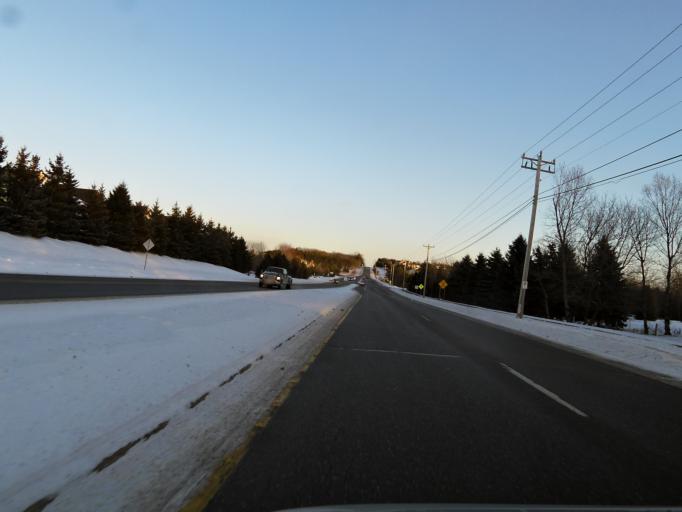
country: US
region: Minnesota
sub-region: Washington County
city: Woodbury
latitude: 44.9198
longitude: -92.8913
